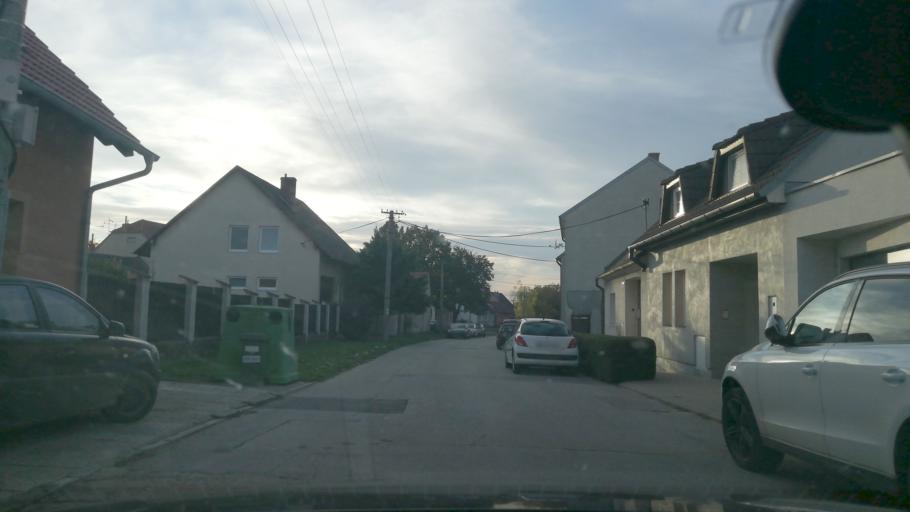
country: SK
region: Trnavsky
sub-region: Okres Skalica
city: Skalica
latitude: 48.8433
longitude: 17.2387
